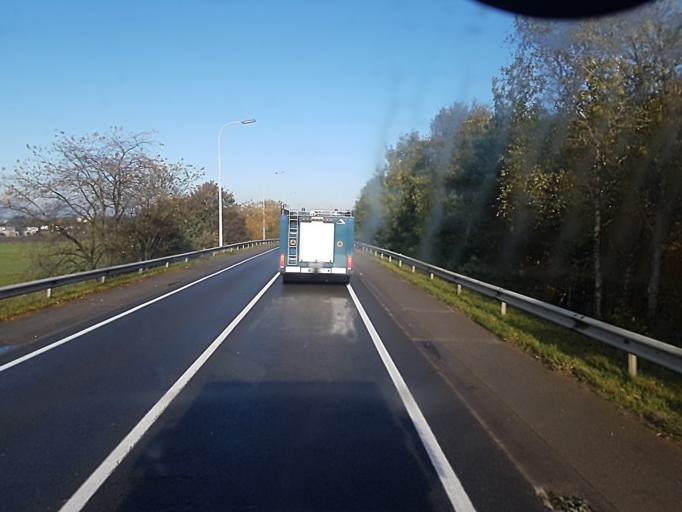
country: BE
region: Flanders
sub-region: Provincie Antwerpen
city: Brecht
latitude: 51.3441
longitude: 4.6726
